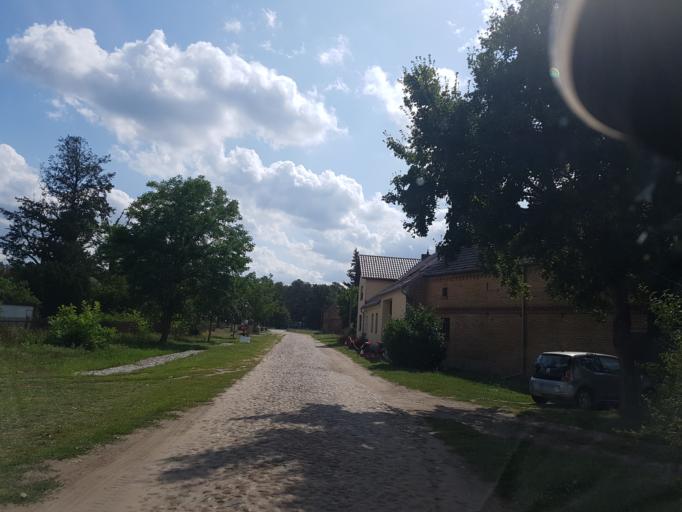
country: DE
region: Brandenburg
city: Fichtenwalde
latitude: 52.2896
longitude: 12.8518
